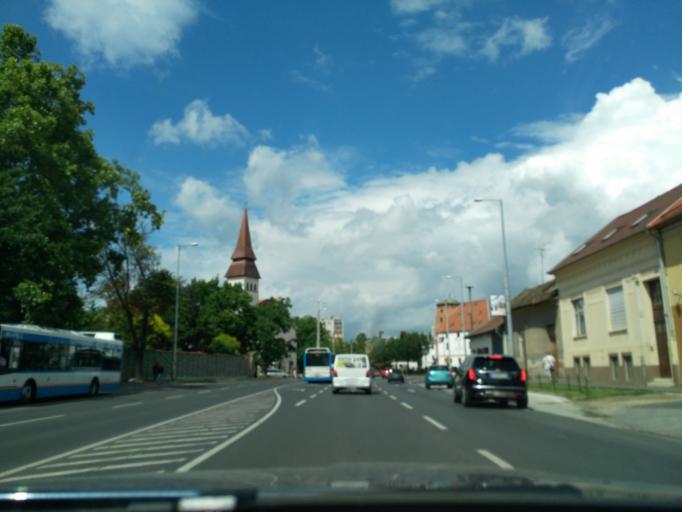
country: HU
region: Hajdu-Bihar
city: Debrecen
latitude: 47.5334
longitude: 21.6117
